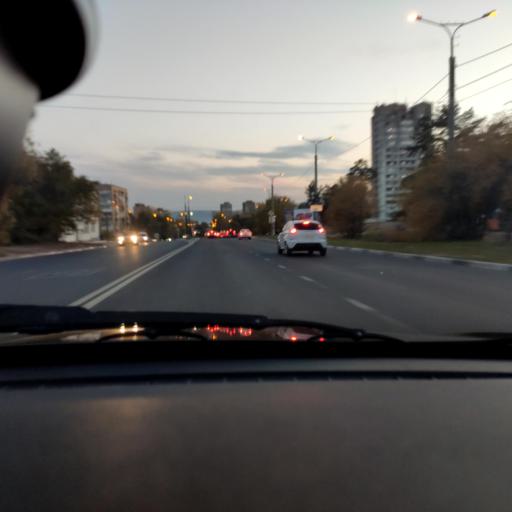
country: RU
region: Samara
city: Zhigulevsk
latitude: 53.4885
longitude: 49.4740
